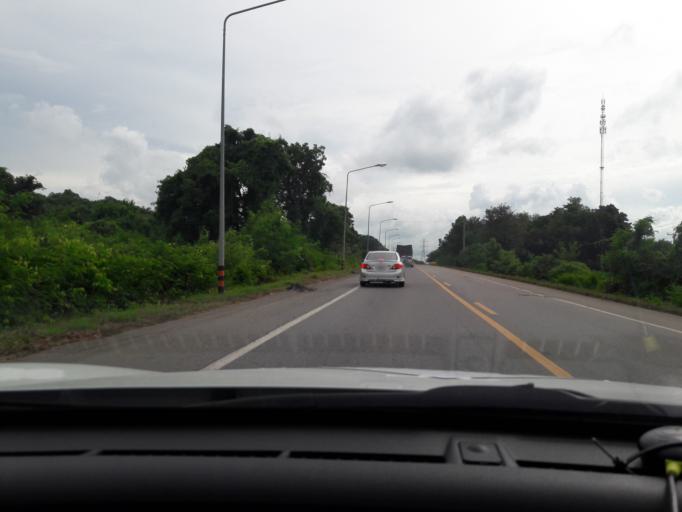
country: TH
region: Nakhon Sawan
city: Tak Fa
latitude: 15.4213
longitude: 100.5169
